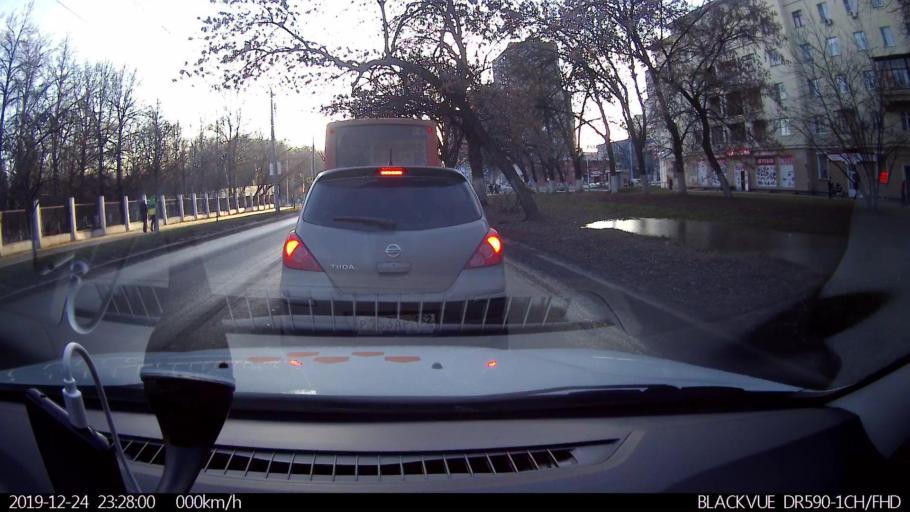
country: RU
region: Nizjnij Novgorod
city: Gorbatovka
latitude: 56.2437
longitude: 43.8496
